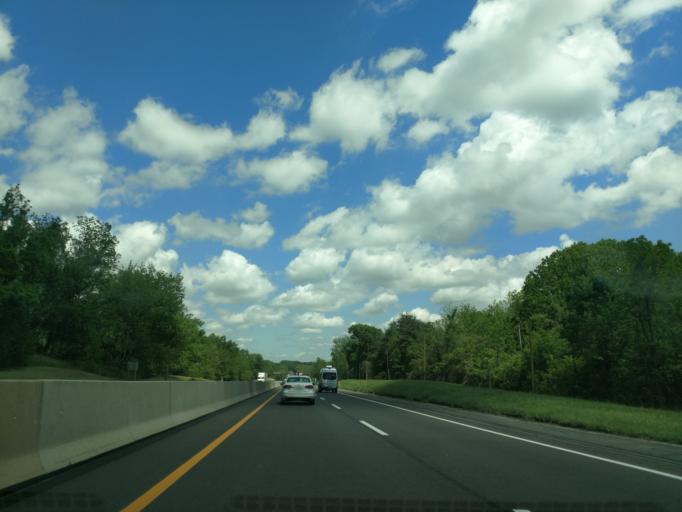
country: US
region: Pennsylvania
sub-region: Chester County
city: Chesterbrook
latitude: 40.0779
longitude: -75.4736
